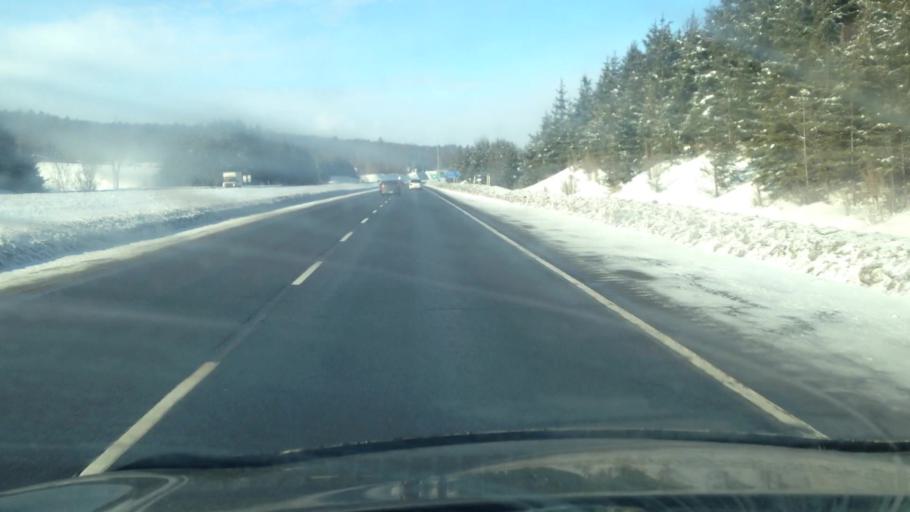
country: CA
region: Quebec
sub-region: Laurentides
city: Prevost
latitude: 45.8343
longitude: -74.0632
